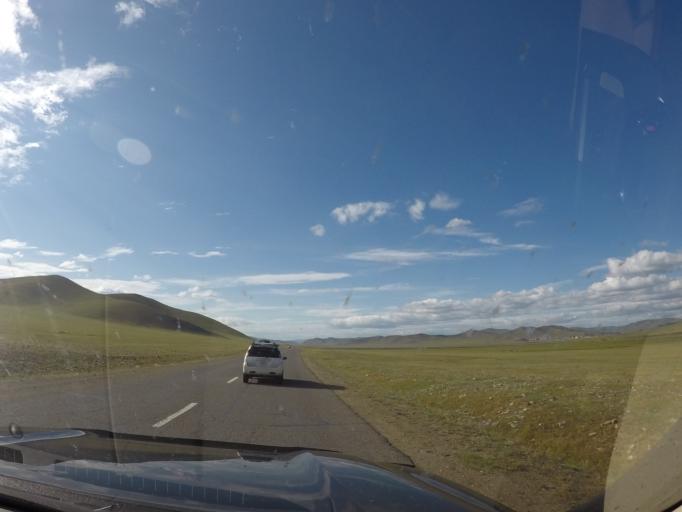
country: MN
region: Hentiy
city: Modot
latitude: 47.7083
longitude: 109.0558
